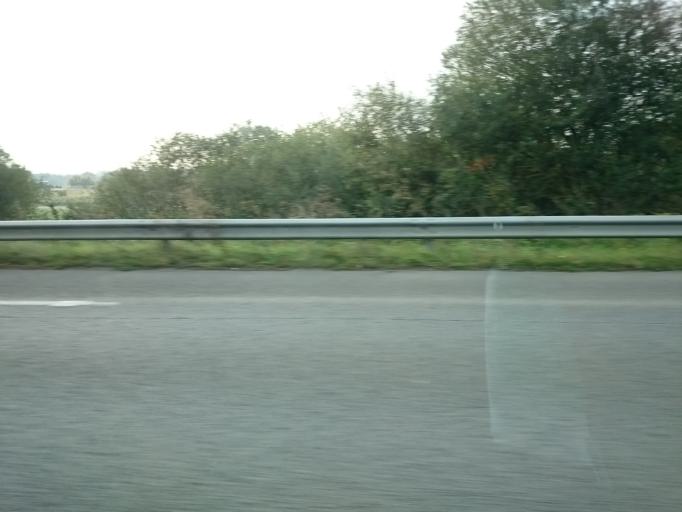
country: FR
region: Pays de la Loire
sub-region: Departement de la Loire-Atlantique
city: La Grigonnais
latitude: 47.5227
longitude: -1.6403
